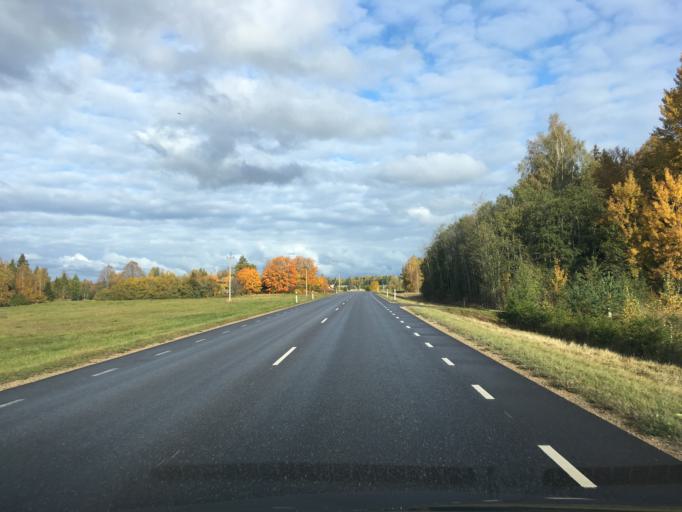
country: EE
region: Harju
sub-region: Raasiku vald
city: Raasiku
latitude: 59.1991
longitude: 25.1839
